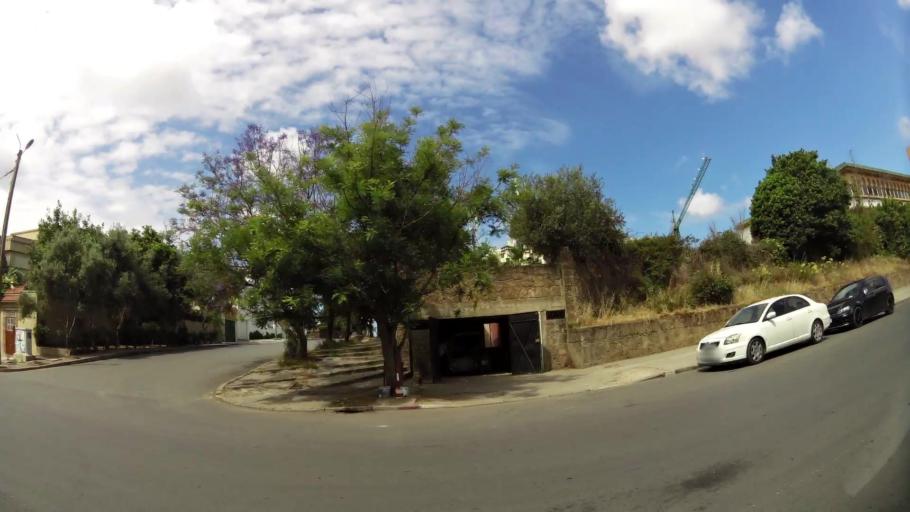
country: MA
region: Gharb-Chrarda-Beni Hssen
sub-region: Kenitra Province
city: Kenitra
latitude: 34.2530
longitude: -6.5956
